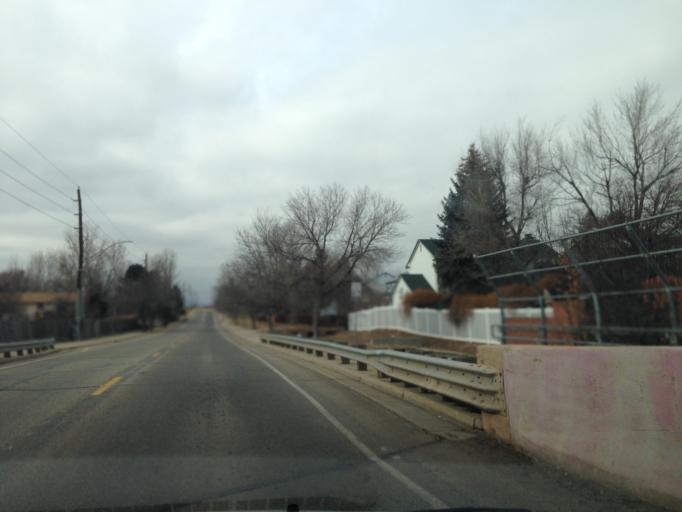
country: US
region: Colorado
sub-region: Boulder County
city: Lafayette
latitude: 39.9942
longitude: -105.1028
